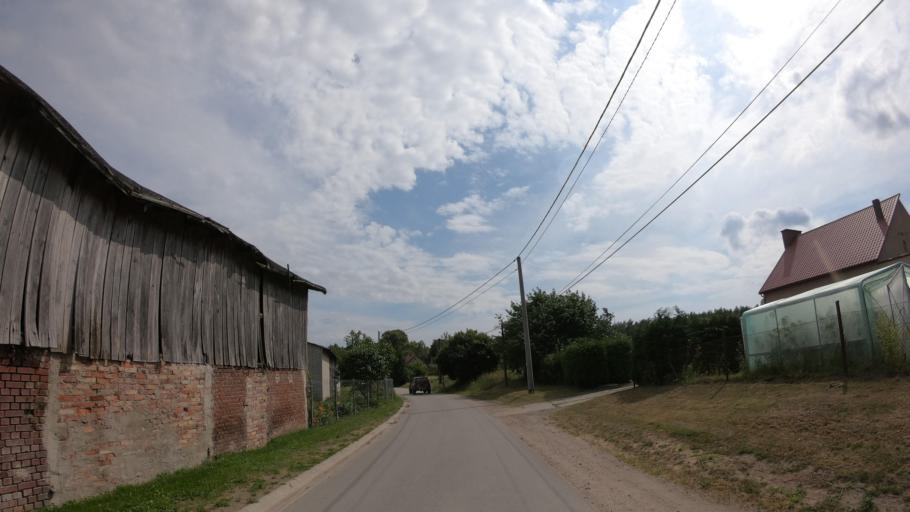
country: PL
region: West Pomeranian Voivodeship
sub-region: Powiat walecki
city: Tuczno
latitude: 53.2330
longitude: 16.1101
